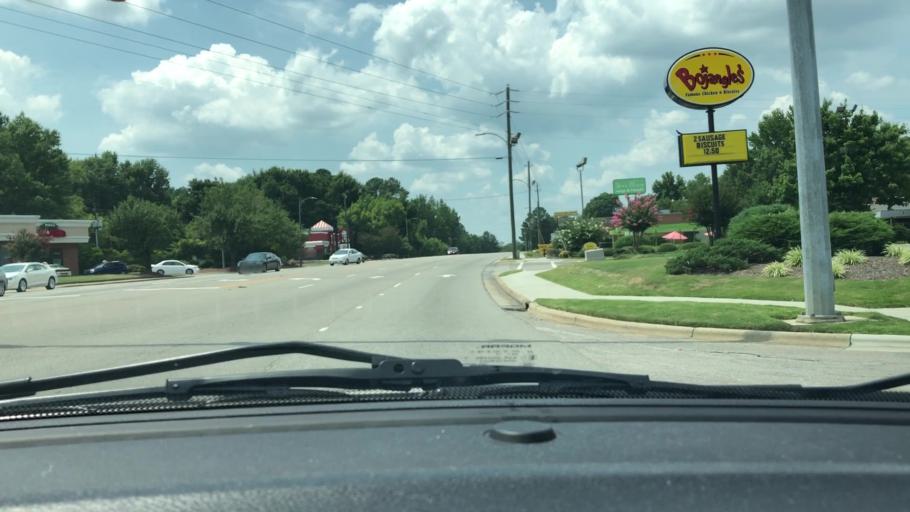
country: US
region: North Carolina
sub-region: Lee County
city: Sanford
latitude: 35.4712
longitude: -79.1727
